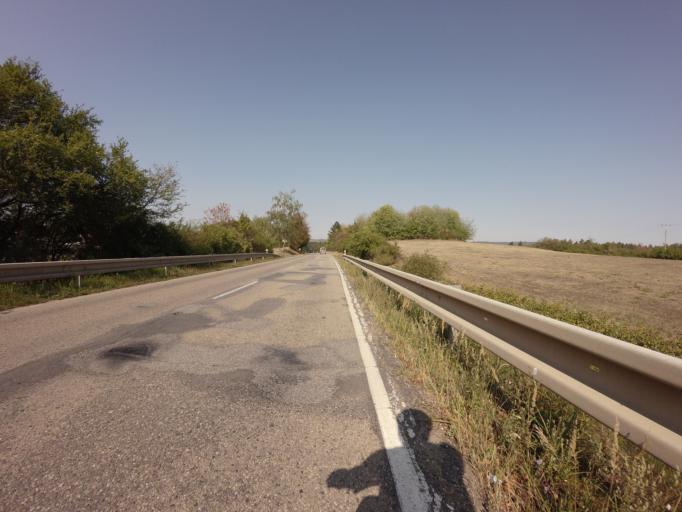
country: CZ
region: Central Bohemia
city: Tynec nad Sazavou
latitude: 49.8263
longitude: 14.6175
